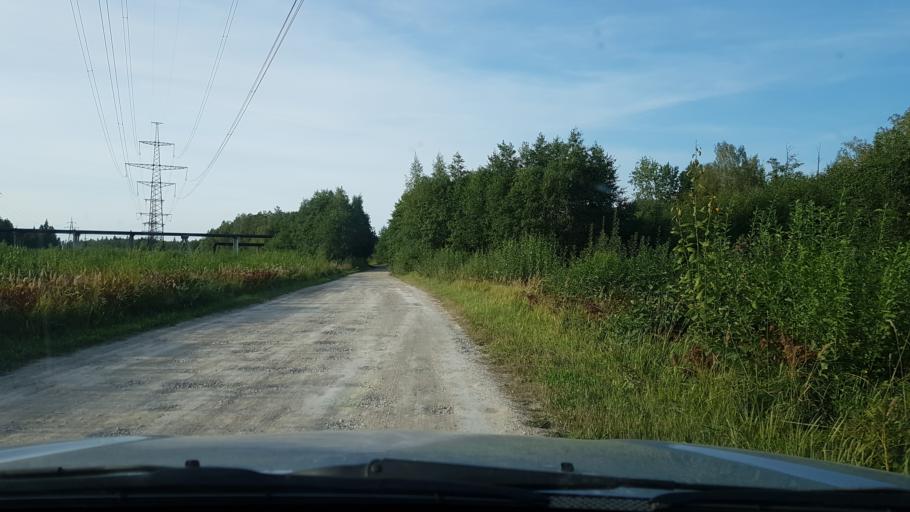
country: EE
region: Ida-Virumaa
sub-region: Sillamaee linn
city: Sillamae
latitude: 59.2754
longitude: 27.9205
